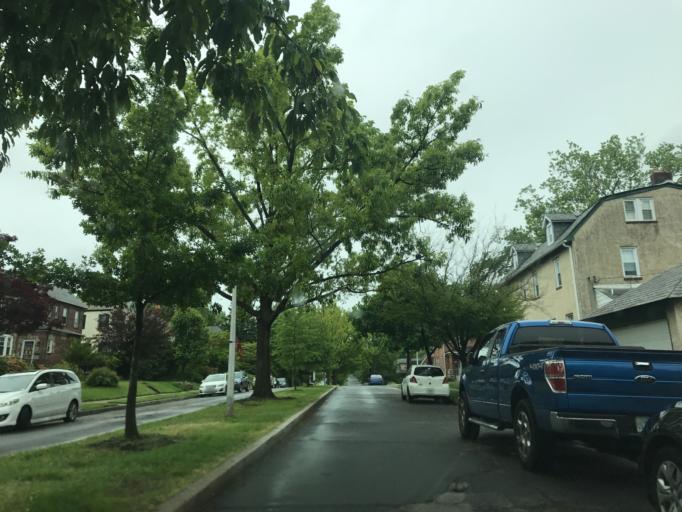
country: US
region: Maryland
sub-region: City of Baltimore
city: Baltimore
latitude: 39.3278
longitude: -76.5761
